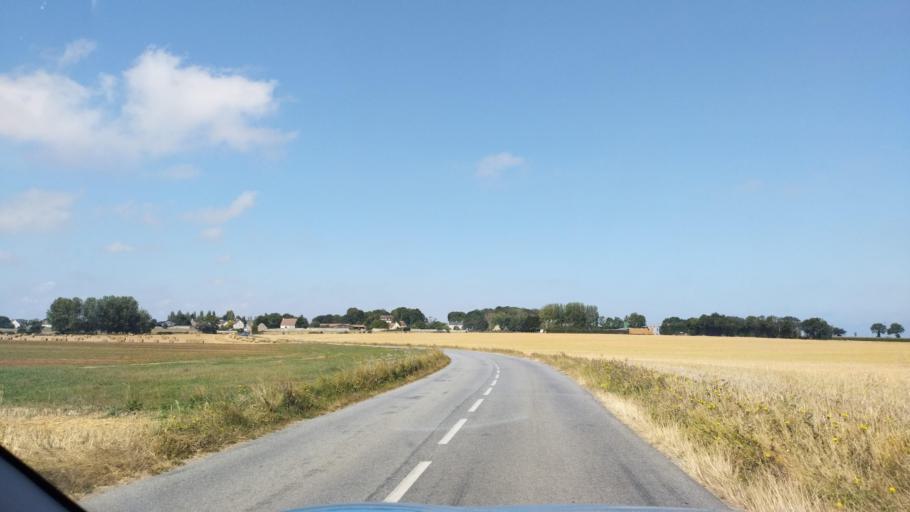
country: FR
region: Lower Normandy
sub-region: Departement du Calvados
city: Douvres-la-Delivrande
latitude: 49.3044
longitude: -0.4003
